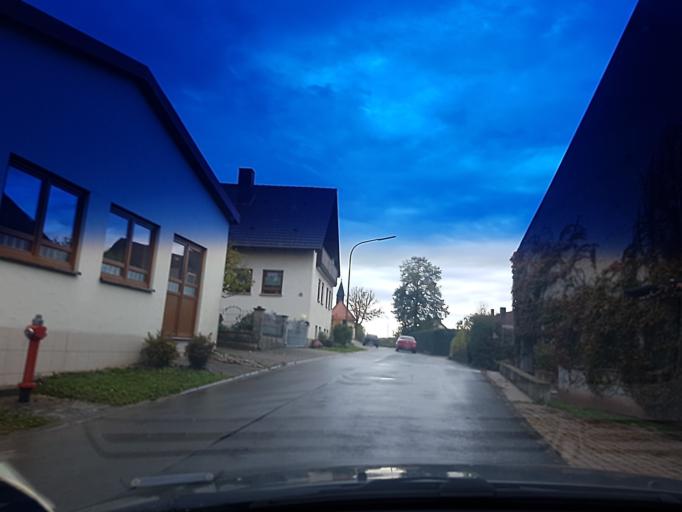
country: DE
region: Bavaria
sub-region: Regierungsbezirk Mittelfranken
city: Burghaslach
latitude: 49.7611
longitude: 10.5682
